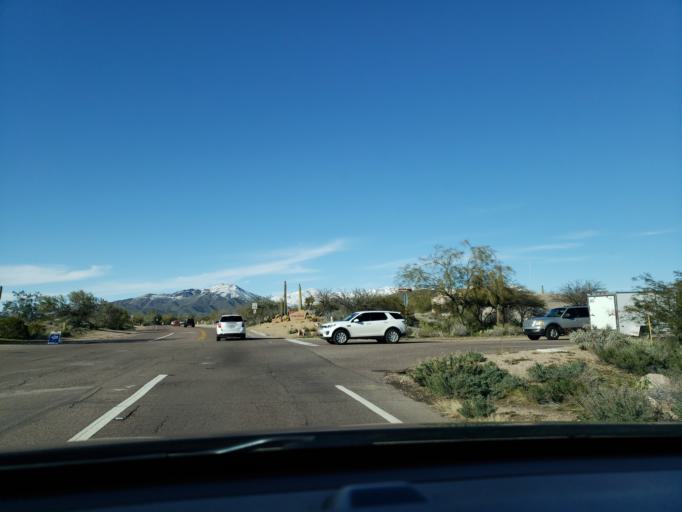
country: US
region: Arizona
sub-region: Maricopa County
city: Carefree
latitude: 33.8136
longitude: -111.8912
